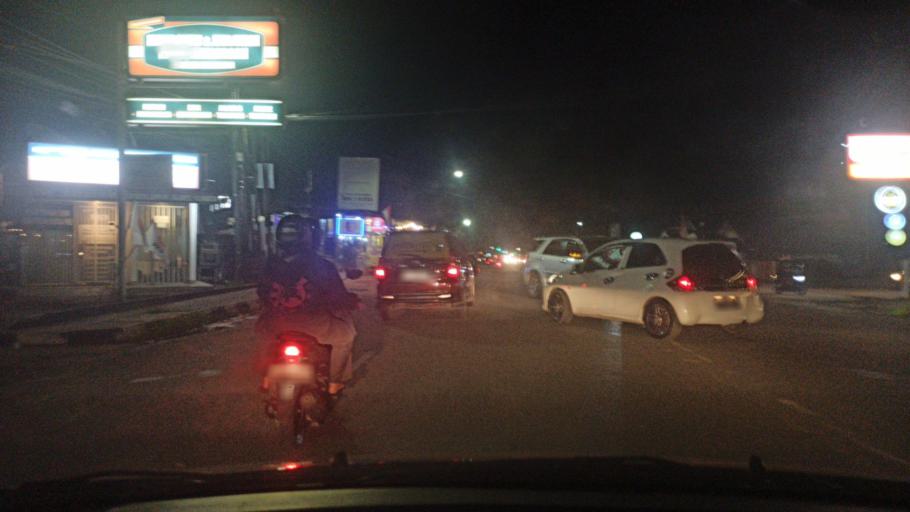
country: ID
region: South Sumatra
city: Plaju
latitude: -2.9913
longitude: 104.7264
